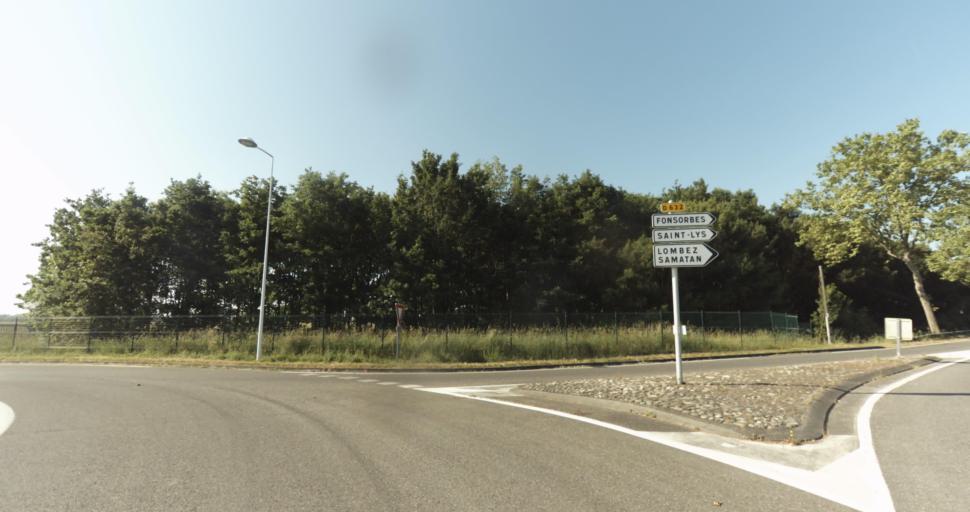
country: FR
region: Midi-Pyrenees
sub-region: Departement de la Haute-Garonne
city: Fonsorbes
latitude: 43.5466
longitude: 1.2506
